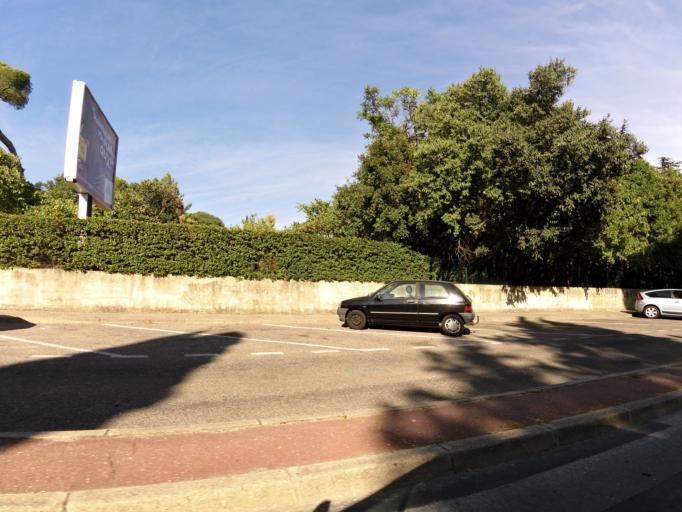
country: FR
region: Languedoc-Roussillon
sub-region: Departement du Gard
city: Nimes
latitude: 43.8401
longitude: 4.3419
